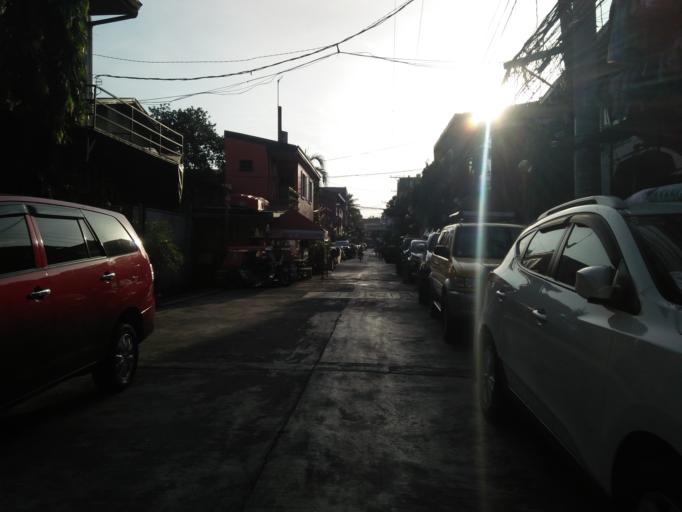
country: PH
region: Metro Manila
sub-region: San Juan
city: San Juan
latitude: 14.6014
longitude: 121.0189
